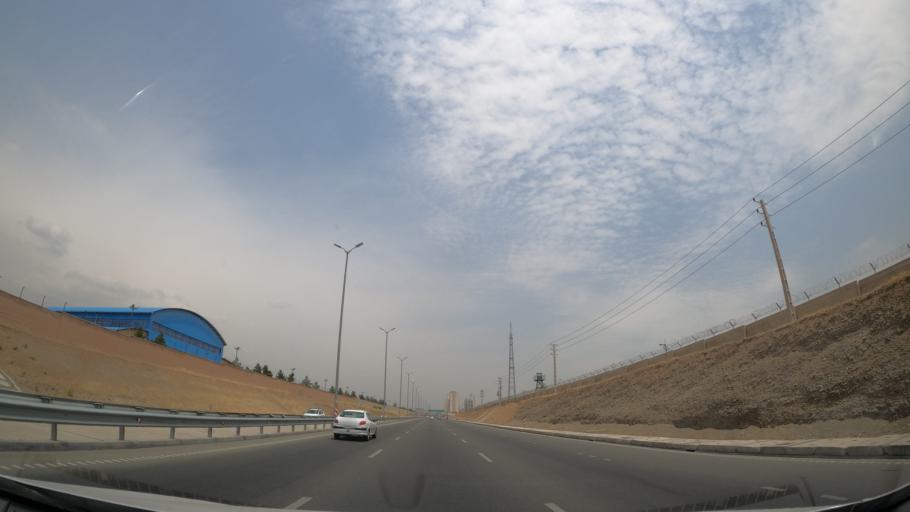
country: IR
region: Tehran
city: Shahr-e Qods
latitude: 35.7398
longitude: 51.2299
